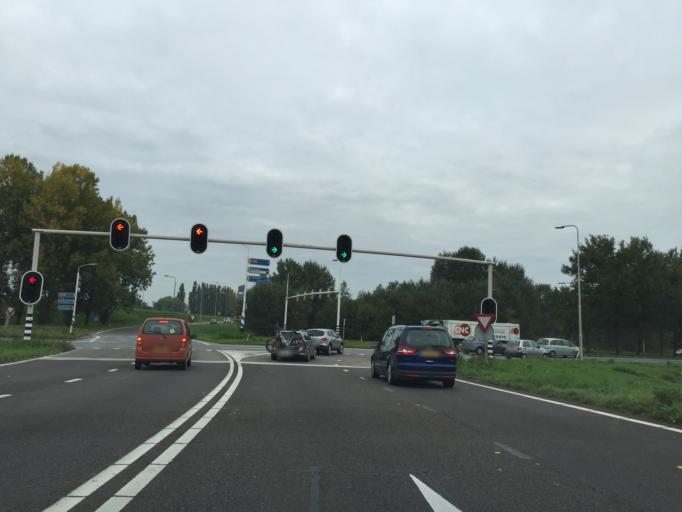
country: NL
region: North Brabant
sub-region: Gemeente Geertruidenberg
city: Geertruidenberg
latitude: 51.6870
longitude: 4.8852
